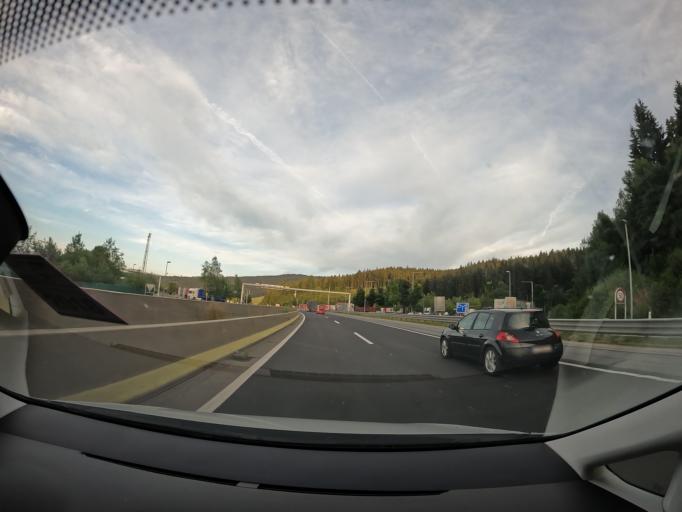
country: AT
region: Styria
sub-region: Politischer Bezirk Voitsberg
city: Voitsberg
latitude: 46.9881
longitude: 15.1074
